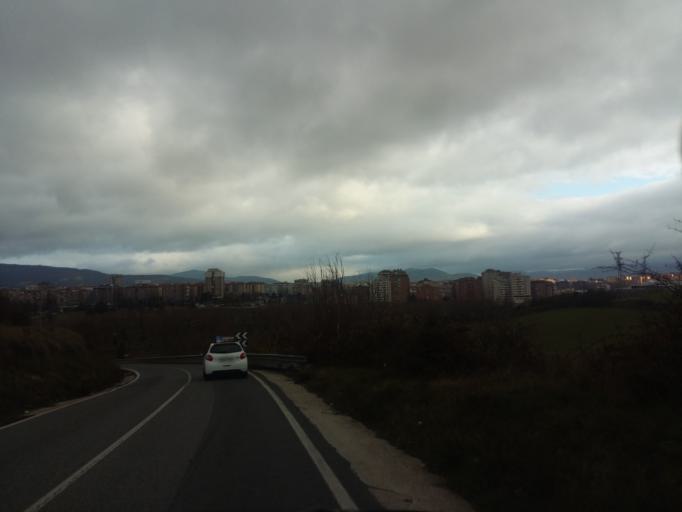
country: ES
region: Navarre
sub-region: Provincia de Navarra
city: Iturrama
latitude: 42.7951
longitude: -1.6519
